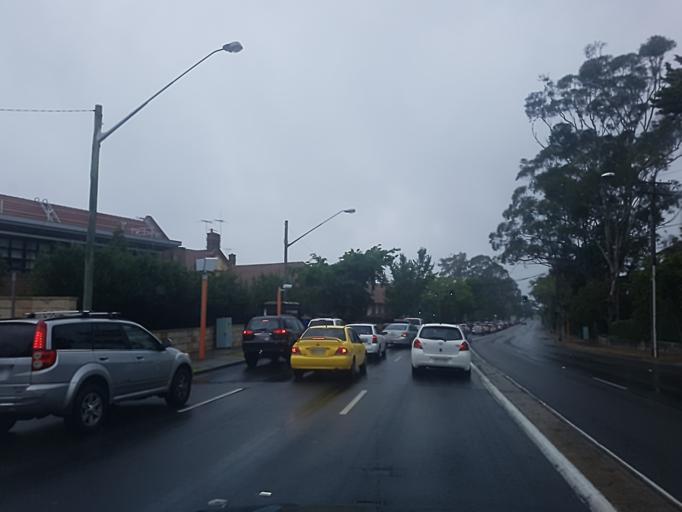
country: AU
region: New South Wales
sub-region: Ku-ring-gai
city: North Wahroonga
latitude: -33.7222
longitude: 151.1182
